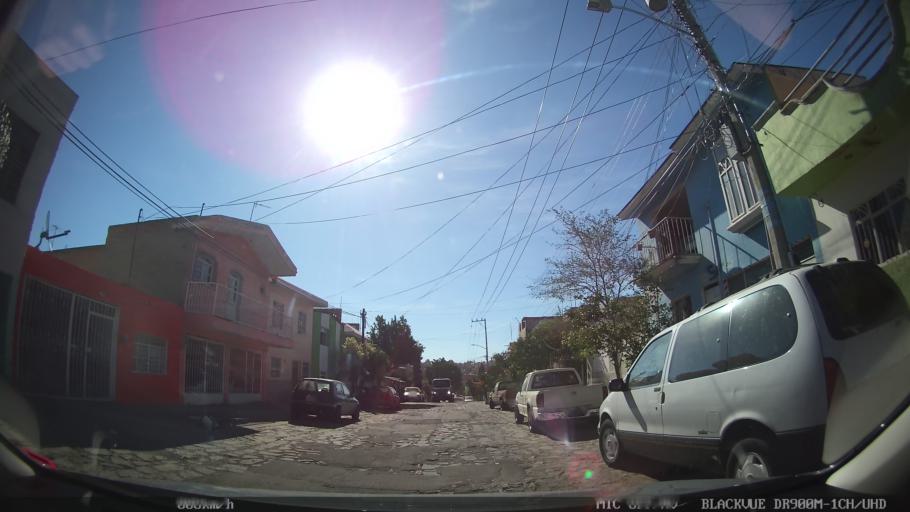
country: MX
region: Jalisco
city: Tlaquepaque
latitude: 20.6873
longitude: -103.2708
